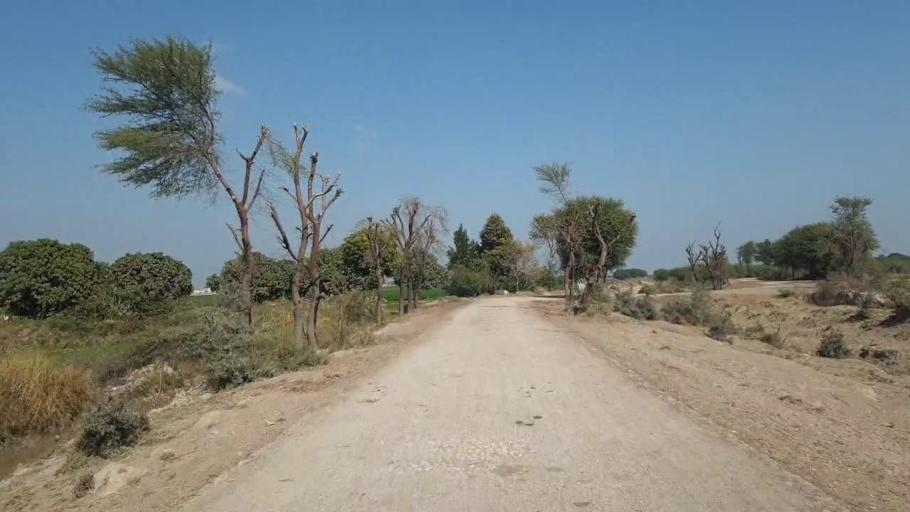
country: PK
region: Sindh
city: Shahpur Chakar
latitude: 26.0559
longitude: 68.5860
